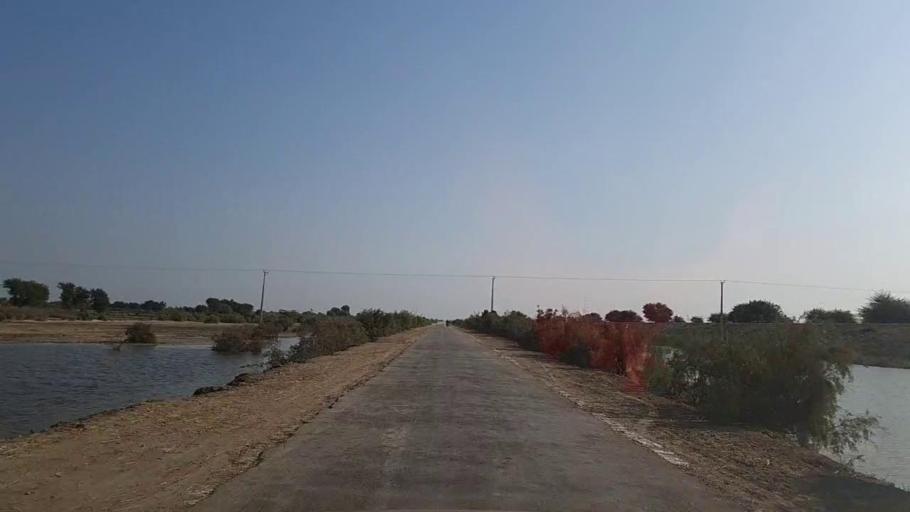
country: PK
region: Sindh
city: Sanghar
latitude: 25.9690
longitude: 69.0328
